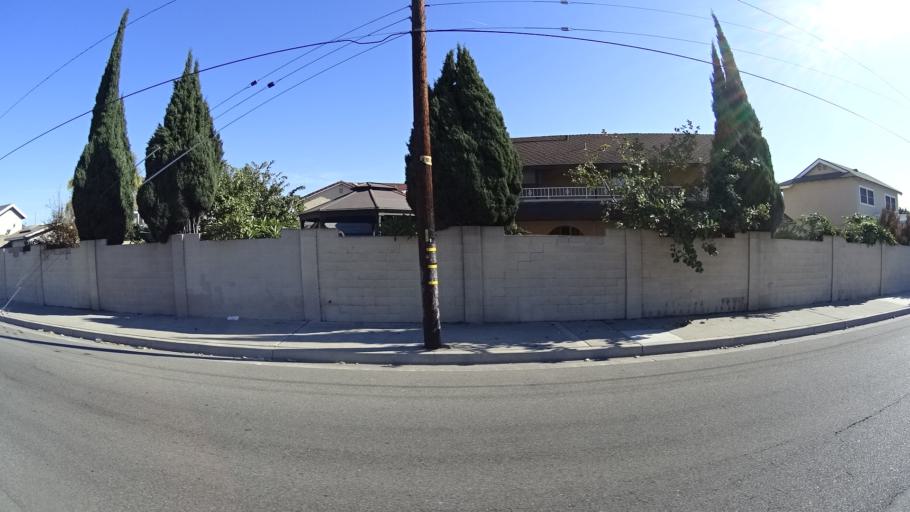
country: US
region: California
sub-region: Orange County
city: Garden Grove
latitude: 33.7472
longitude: -117.9548
